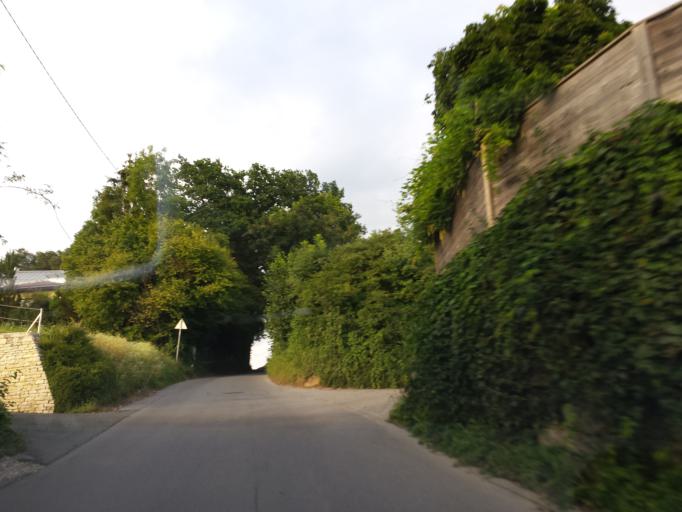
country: AT
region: Styria
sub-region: Politischer Bezirk Graz-Umgebung
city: Stattegg
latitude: 47.1251
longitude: 15.4365
